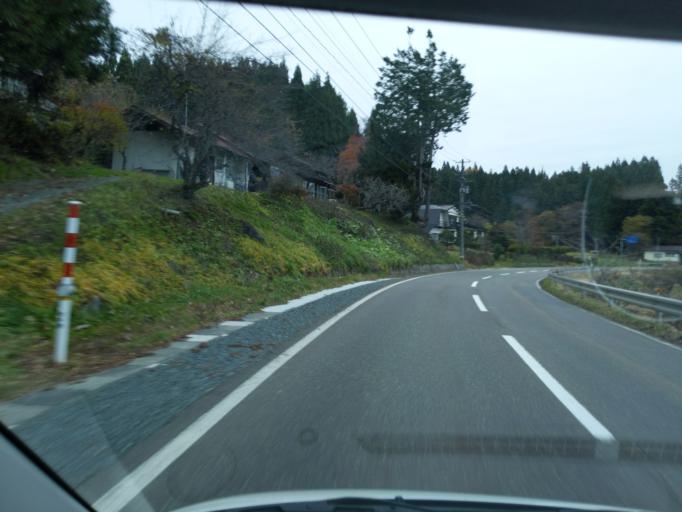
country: JP
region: Iwate
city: Kitakami
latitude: 39.2328
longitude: 141.2975
